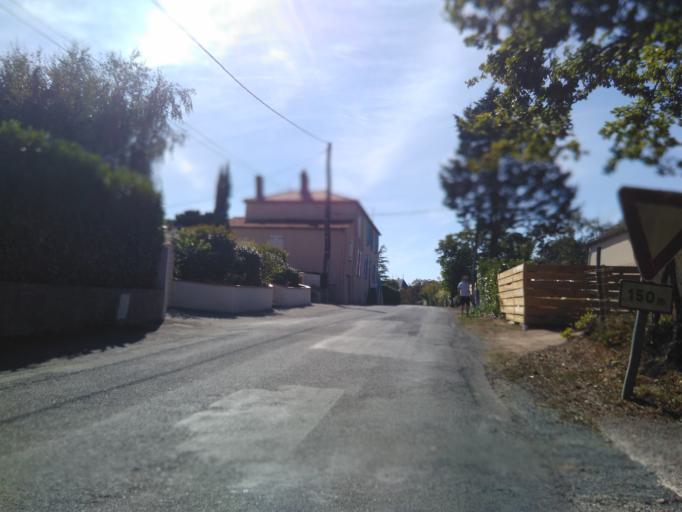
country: FR
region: Pays de la Loire
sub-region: Departement de la Vendee
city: La Chaize-le-Vicomte
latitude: 46.6714
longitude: -1.2886
